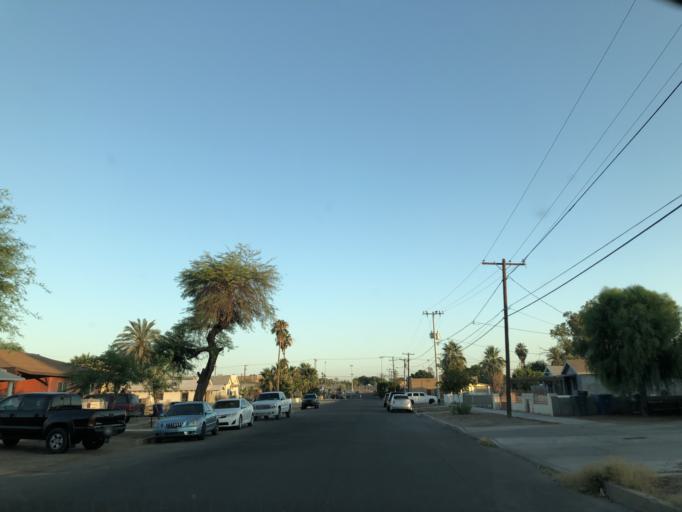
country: US
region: Arizona
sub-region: Yuma County
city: Yuma
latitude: 32.7230
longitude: -114.6308
